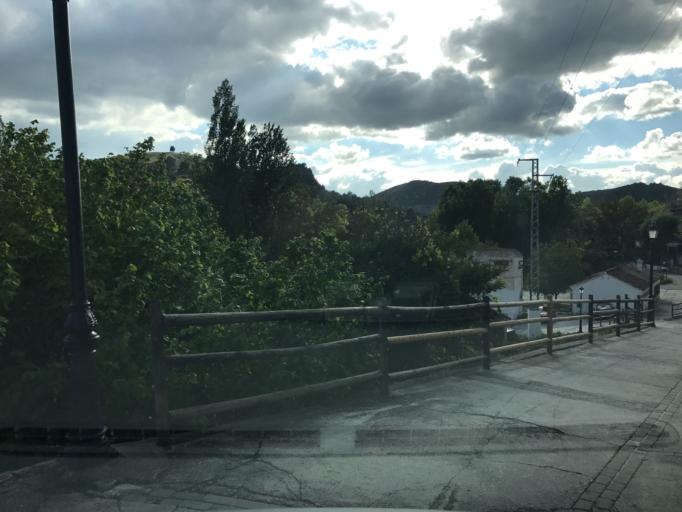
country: ES
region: Andalusia
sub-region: Provincia de Granada
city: Diezma
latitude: 37.2403
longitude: -3.3705
